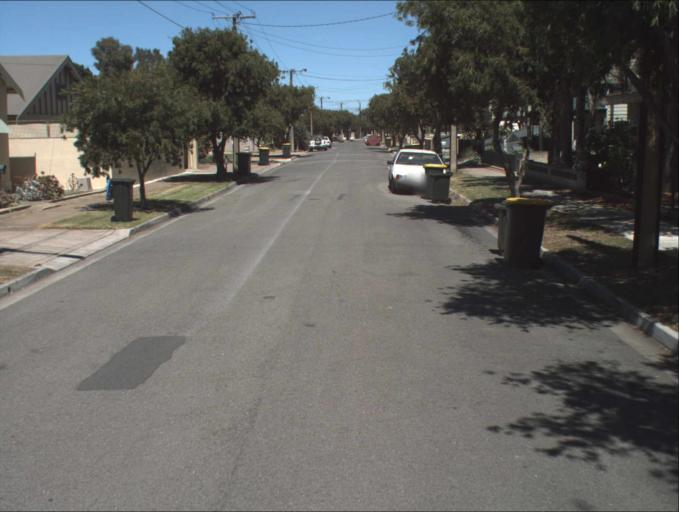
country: AU
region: South Australia
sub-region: Port Adelaide Enfield
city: Birkenhead
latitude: -34.8469
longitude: 138.4925
